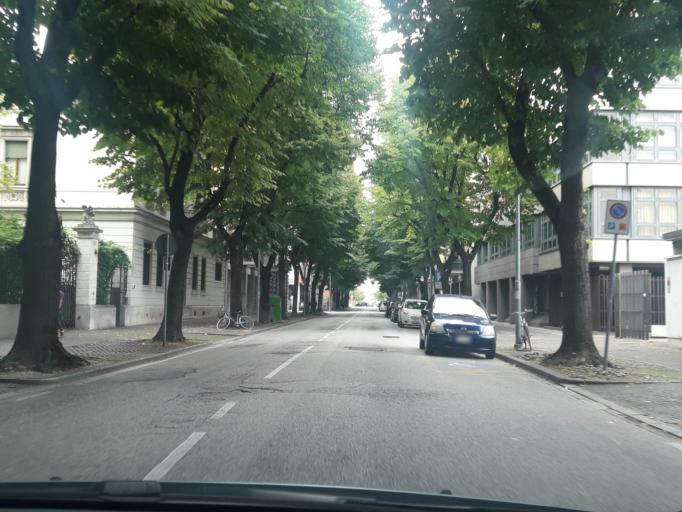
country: IT
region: Friuli Venezia Giulia
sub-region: Provincia di Udine
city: Udine
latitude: 46.0560
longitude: 13.2390
